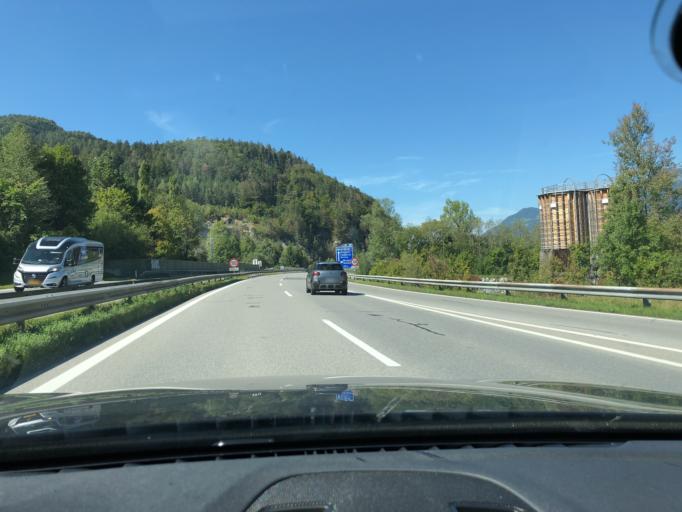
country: AT
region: Vorarlberg
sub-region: Politischer Bezirk Bludenz
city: Nuziders
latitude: 47.1593
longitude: 9.8011
